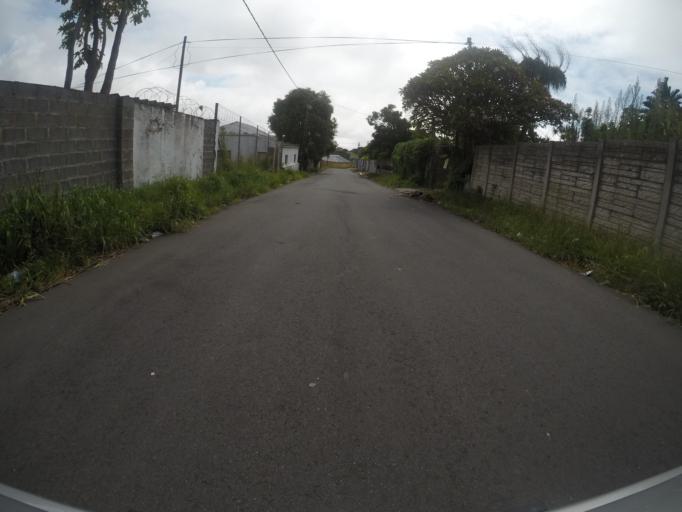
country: ZA
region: Eastern Cape
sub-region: Buffalo City Metropolitan Municipality
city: East London
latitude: -32.9975
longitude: 27.9068
